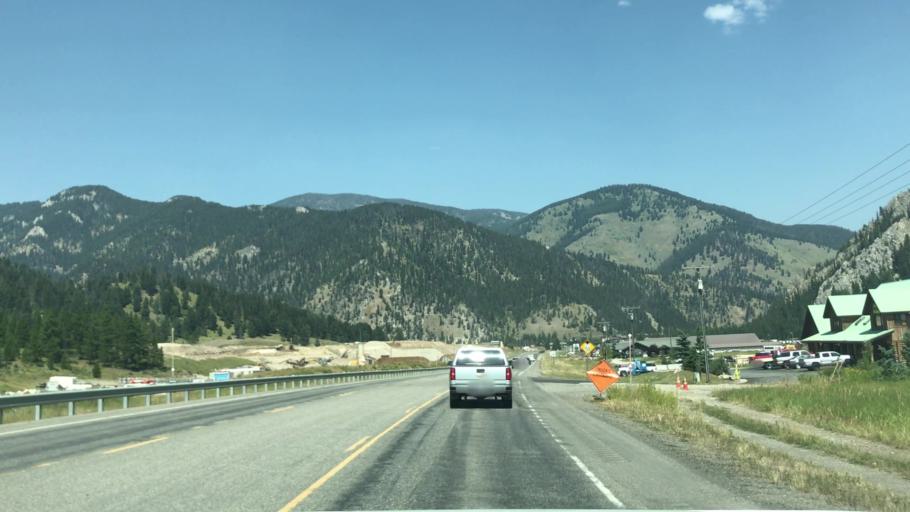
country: US
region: Montana
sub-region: Gallatin County
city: Big Sky
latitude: 45.2538
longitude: -111.2543
